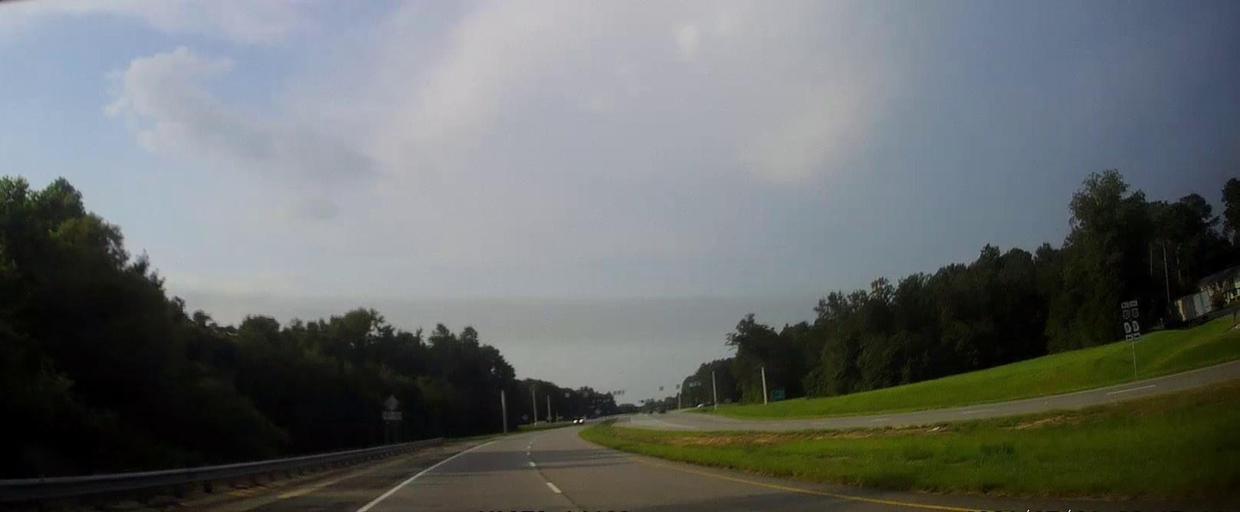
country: US
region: Georgia
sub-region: Laurens County
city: Dublin
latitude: 32.5482
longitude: -82.9786
